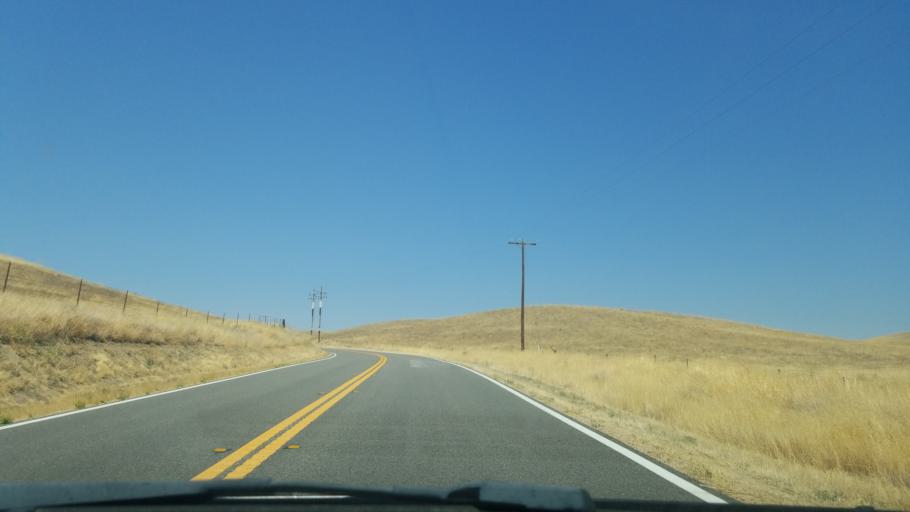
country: US
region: California
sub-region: San Luis Obispo County
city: Shandon
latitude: 35.5975
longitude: -120.4149
